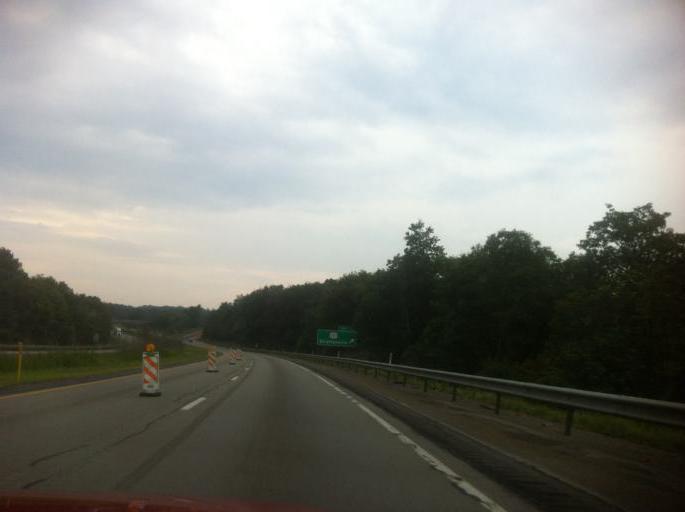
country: US
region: Pennsylvania
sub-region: Clarion County
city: Clarion
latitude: 41.1867
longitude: -79.2391
